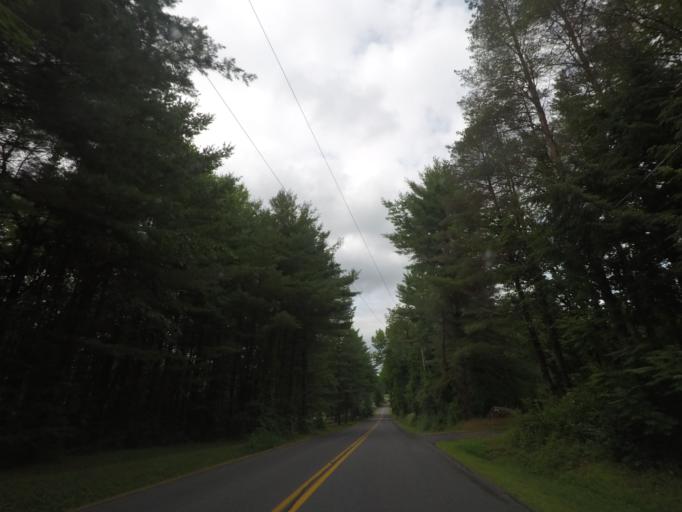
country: US
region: New York
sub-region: Saratoga County
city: Stillwater
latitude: 42.9970
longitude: -73.6930
